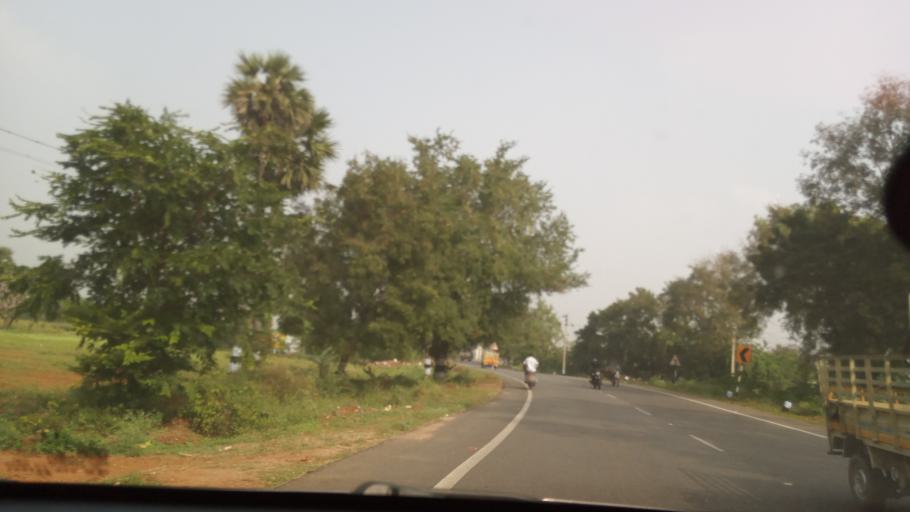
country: IN
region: Tamil Nadu
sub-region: Erode
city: Punjai Puliyampatti
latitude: 11.3684
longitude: 77.1713
